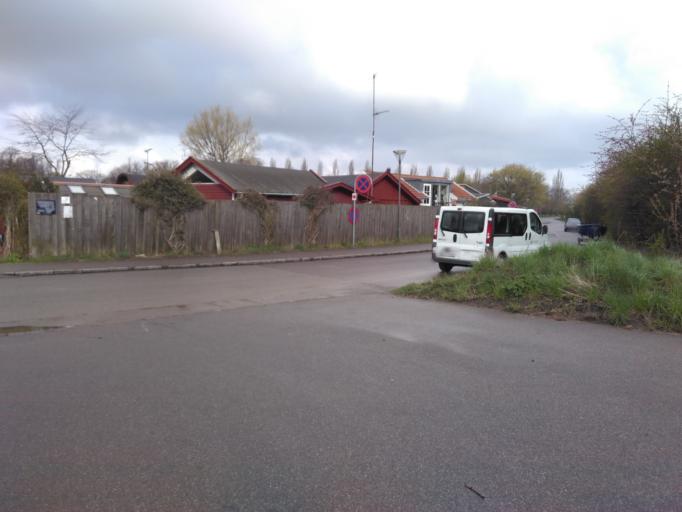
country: DK
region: Capital Region
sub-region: Frederiksberg Kommune
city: Frederiksberg
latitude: 55.6435
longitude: 12.5263
